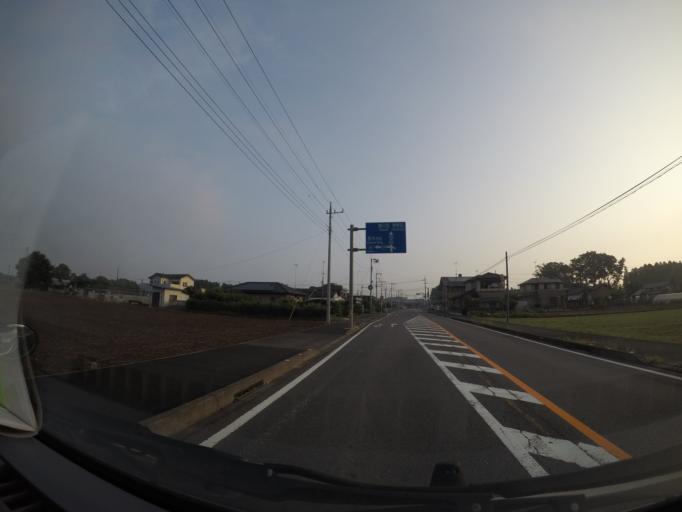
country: JP
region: Ibaraki
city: Koga
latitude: 36.2284
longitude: 139.7696
